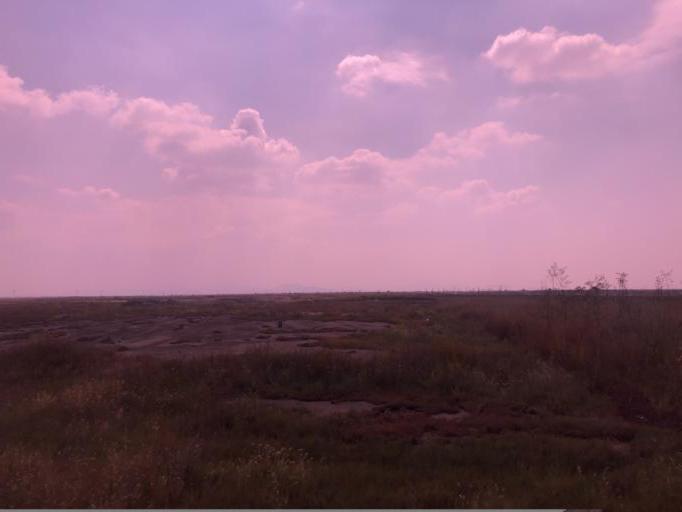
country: MX
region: Mexico
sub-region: Atenco
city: Colonia el Salado
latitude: 19.5519
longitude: -98.9892
